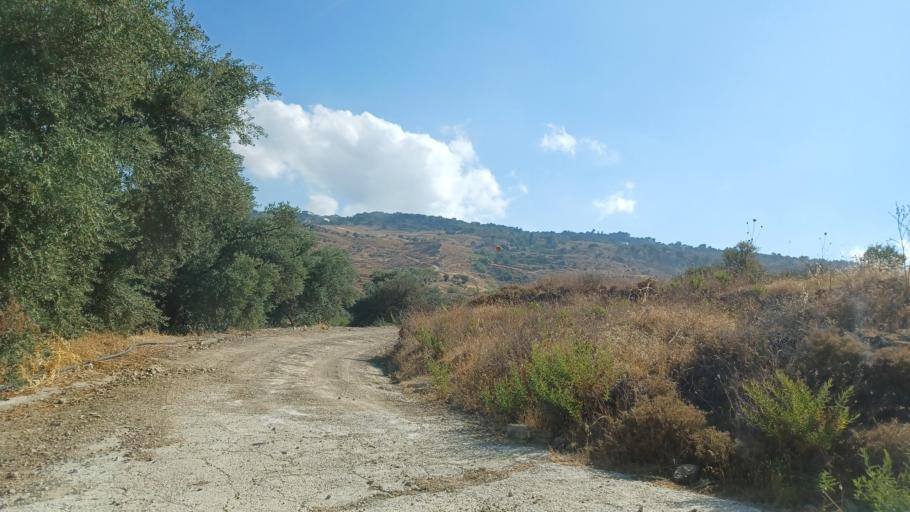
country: CY
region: Pafos
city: Mesogi
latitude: 34.8790
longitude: 32.6011
